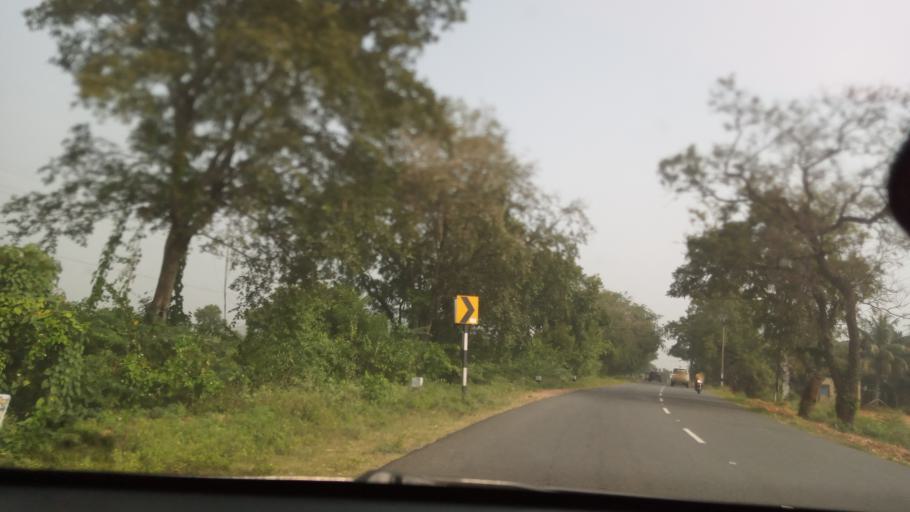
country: IN
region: Tamil Nadu
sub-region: Erode
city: Punjai Puliyampatti
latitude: 11.3249
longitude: 77.1484
